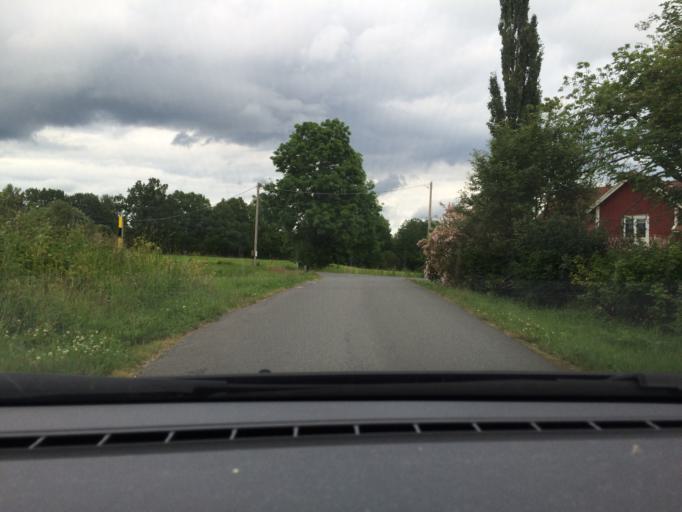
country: SE
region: Joenkoeping
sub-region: Varnamo Kommun
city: Varnamo
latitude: 57.1870
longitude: 13.9401
